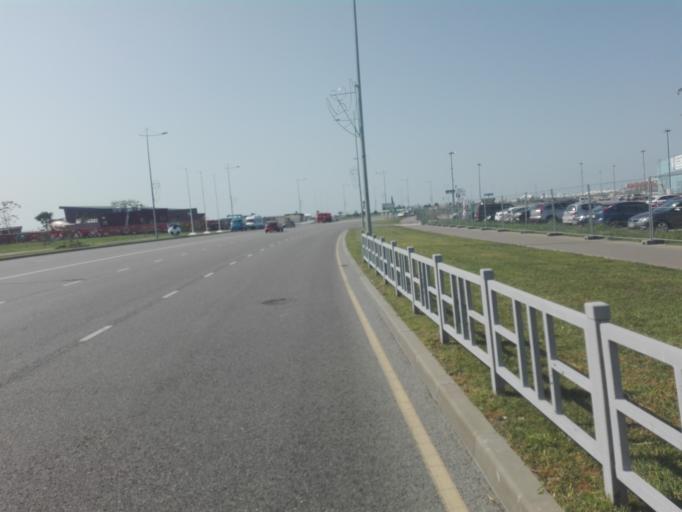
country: RU
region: Krasnodarskiy
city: Adler
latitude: 43.3996
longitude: 39.9526
